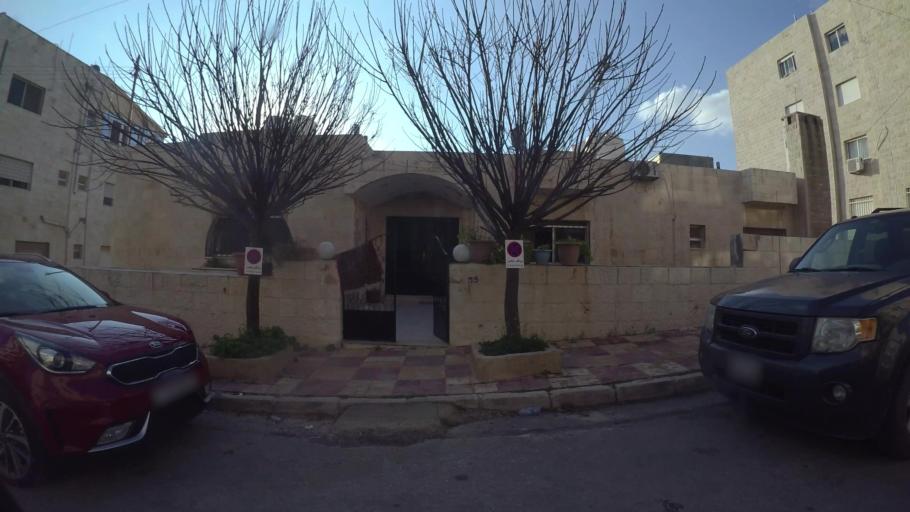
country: JO
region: Amman
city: Al Jubayhah
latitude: 31.9962
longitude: 35.8670
